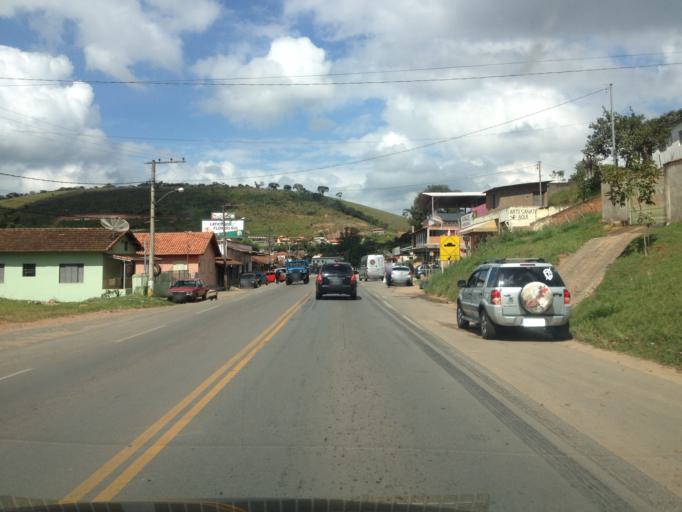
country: BR
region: Minas Gerais
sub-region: Itanhandu
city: Itanhandu
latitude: -22.1935
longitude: -44.9754
